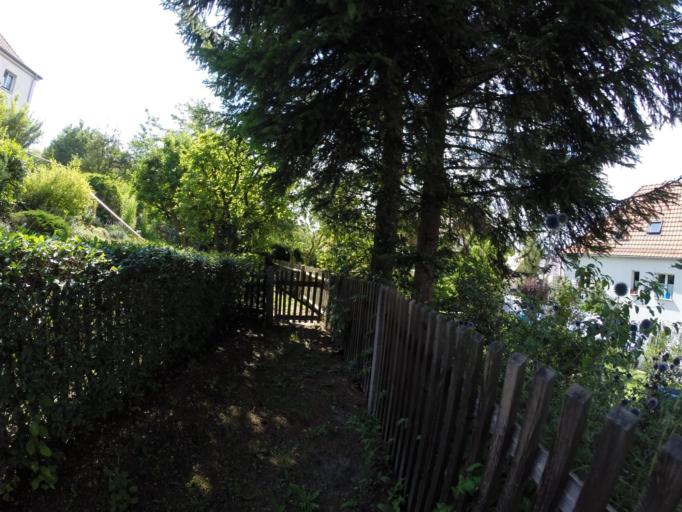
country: DE
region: Thuringia
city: Jena
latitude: 50.9223
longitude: 11.5995
